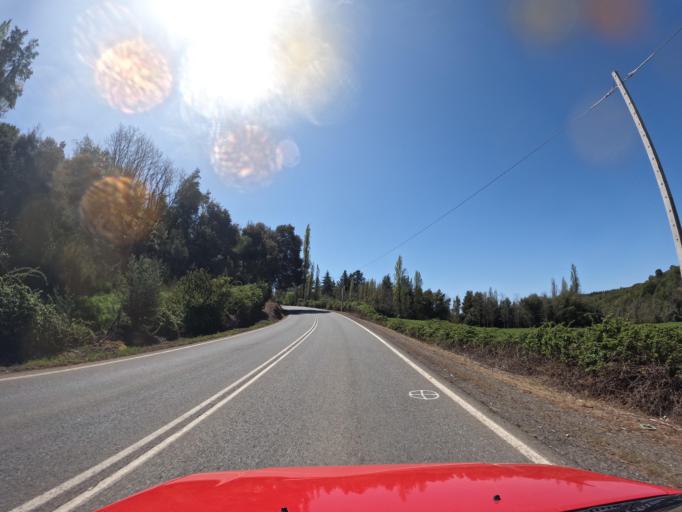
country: CL
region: Maule
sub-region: Provincia de Talca
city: San Clemente
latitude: -35.4563
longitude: -71.2691
